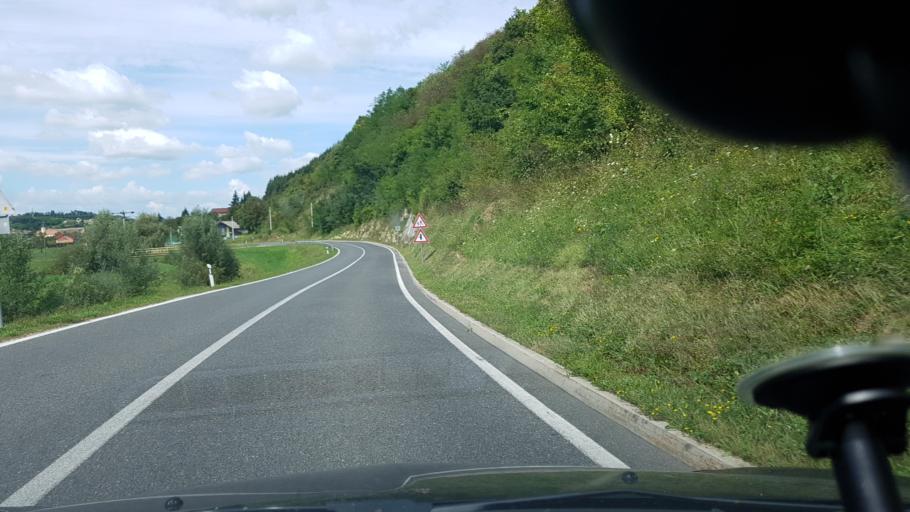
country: HR
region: Varazdinska
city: Lepoglava
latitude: 46.2190
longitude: 15.9969
